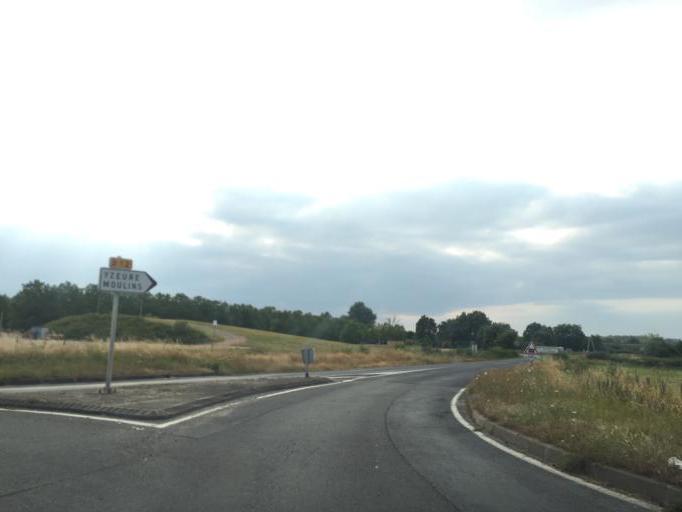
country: FR
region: Auvergne
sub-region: Departement de l'Allier
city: Toulon-sur-Allier
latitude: 46.5379
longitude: 3.3832
